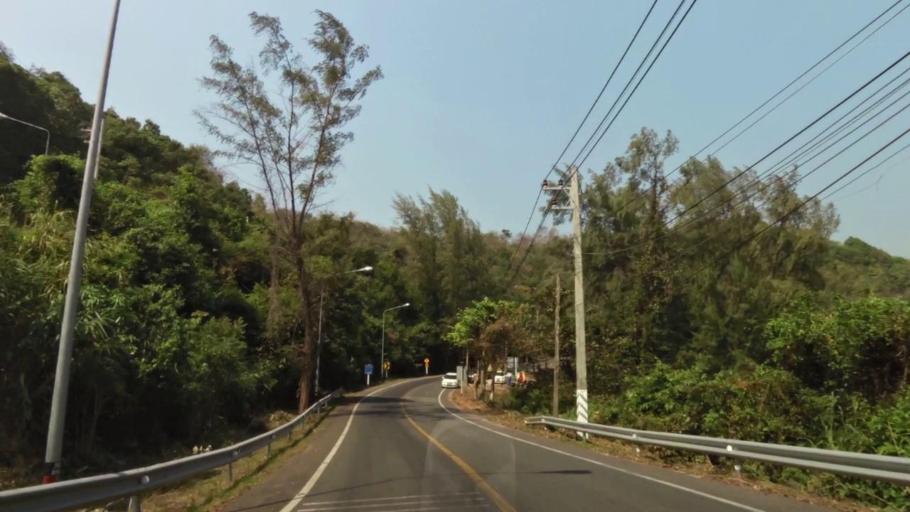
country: TH
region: Chanthaburi
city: Tha Mai
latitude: 12.5244
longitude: 101.9484
